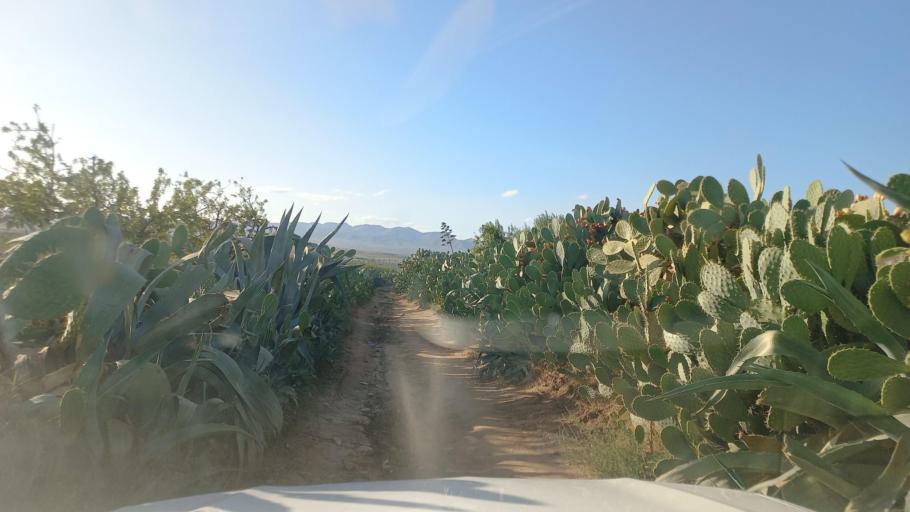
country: TN
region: Al Qasrayn
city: Sbiba
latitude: 35.3846
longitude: 9.1573
